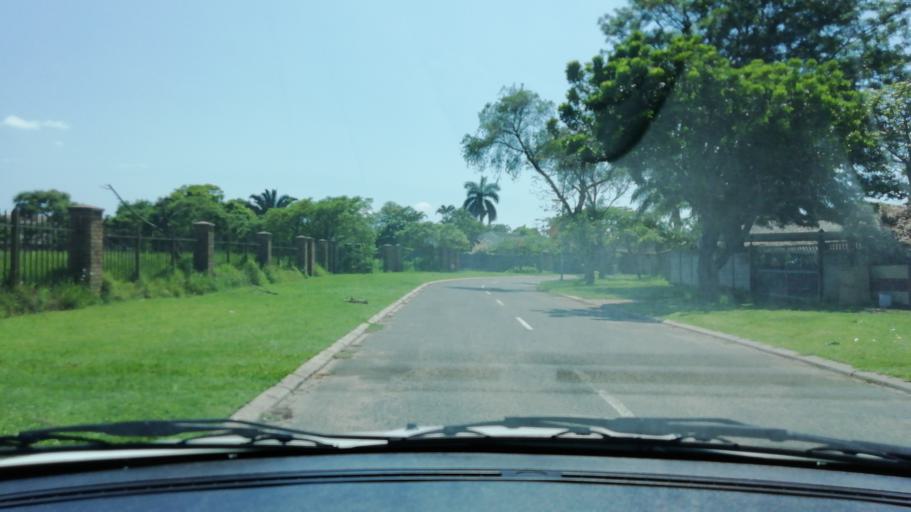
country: ZA
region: KwaZulu-Natal
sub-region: uThungulu District Municipality
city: Richards Bay
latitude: -28.7405
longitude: 32.0562
